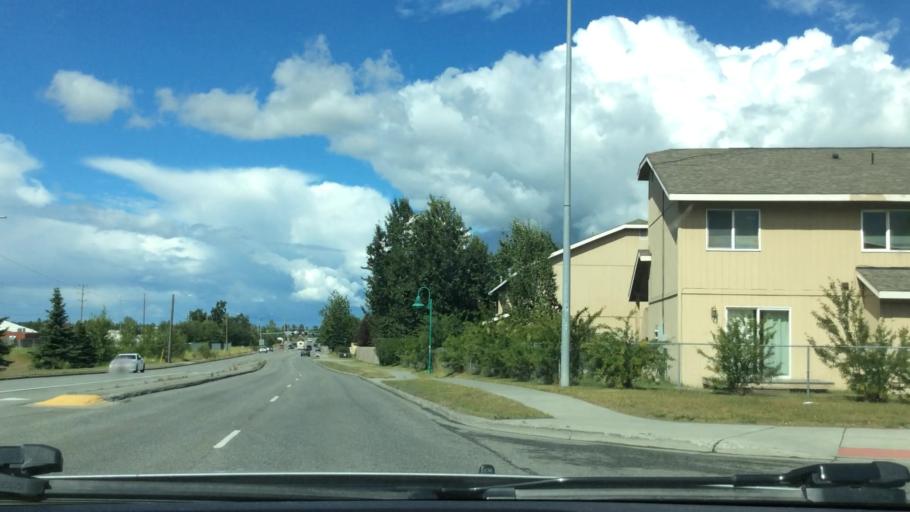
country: US
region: Alaska
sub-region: Anchorage Municipality
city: Anchorage
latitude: 61.2126
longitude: -149.8082
